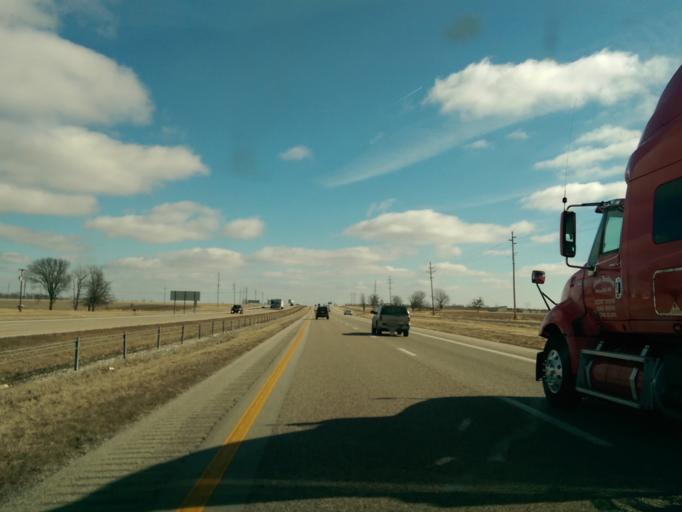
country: US
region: Missouri
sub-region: Montgomery County
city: Montgomery City
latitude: 38.8956
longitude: -91.4424
